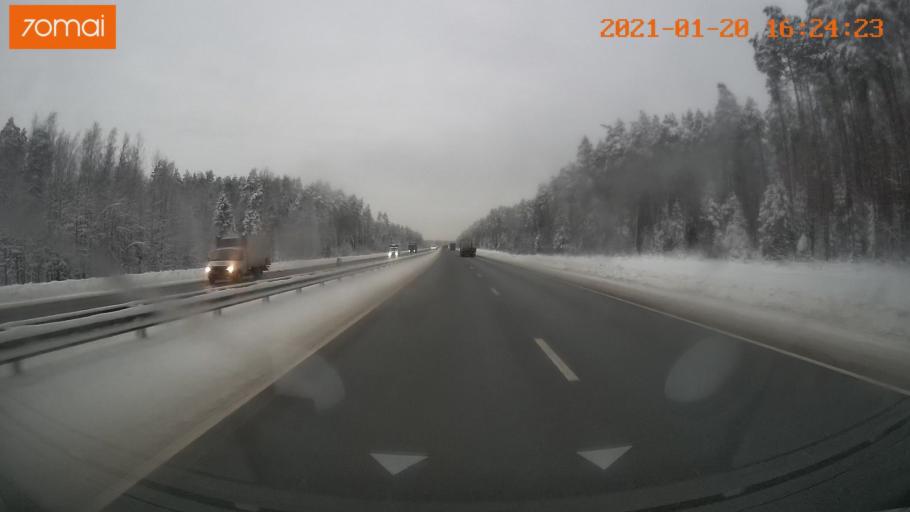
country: RU
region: Vladimir
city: Kameshkovo
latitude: 56.1784
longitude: 40.9465
